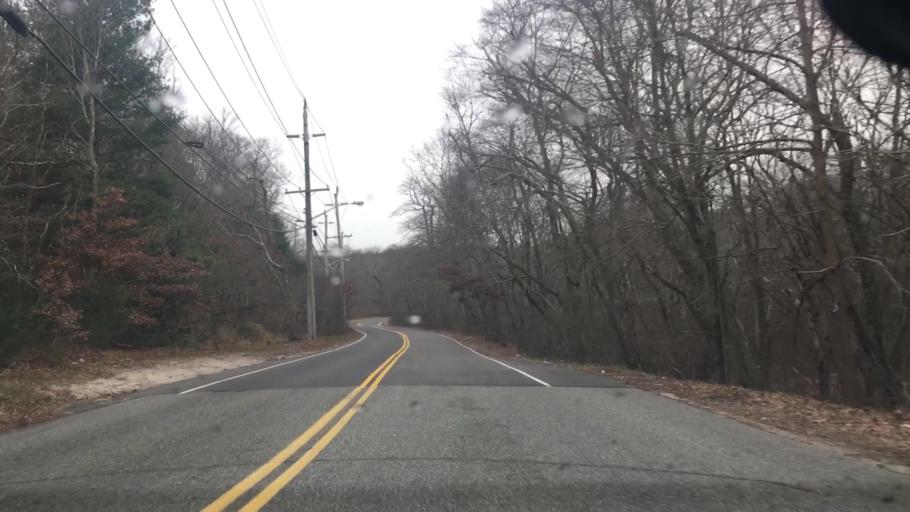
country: US
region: New York
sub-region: Suffolk County
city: Middle Island
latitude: 40.8636
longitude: -72.9400
